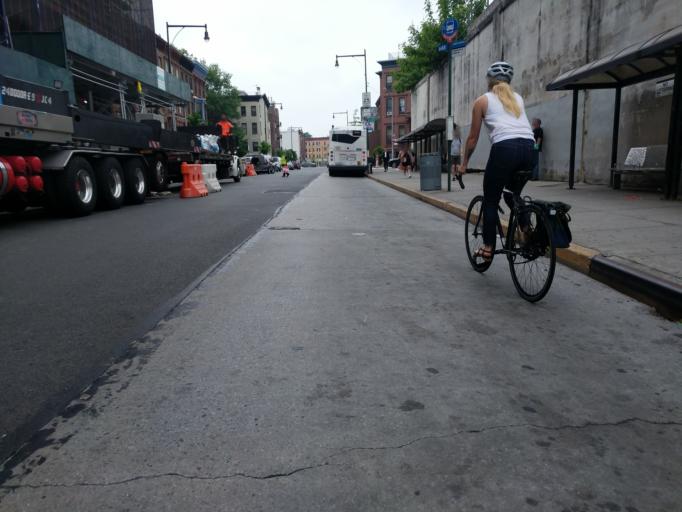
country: US
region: New York
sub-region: Kings County
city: Brooklyn
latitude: 40.6808
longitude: -73.9556
